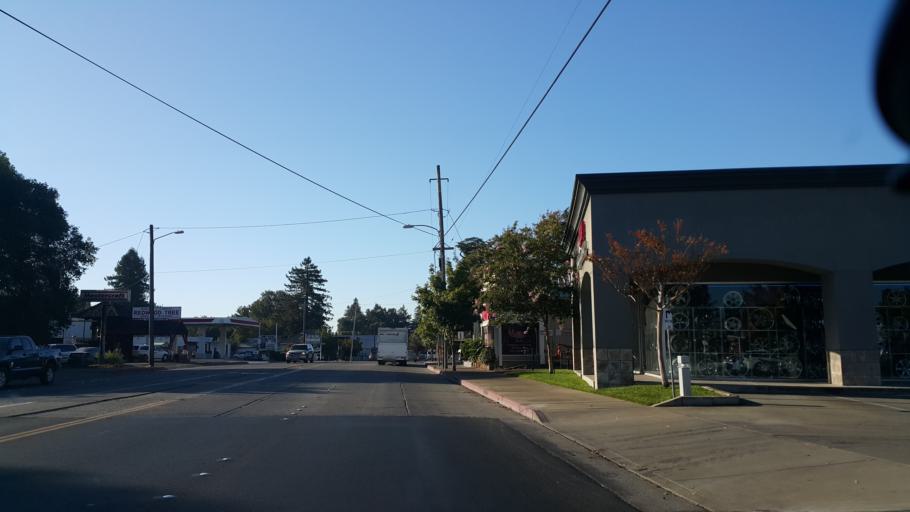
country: US
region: California
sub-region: Mendocino County
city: Ukiah
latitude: 39.1592
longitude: -123.2089
